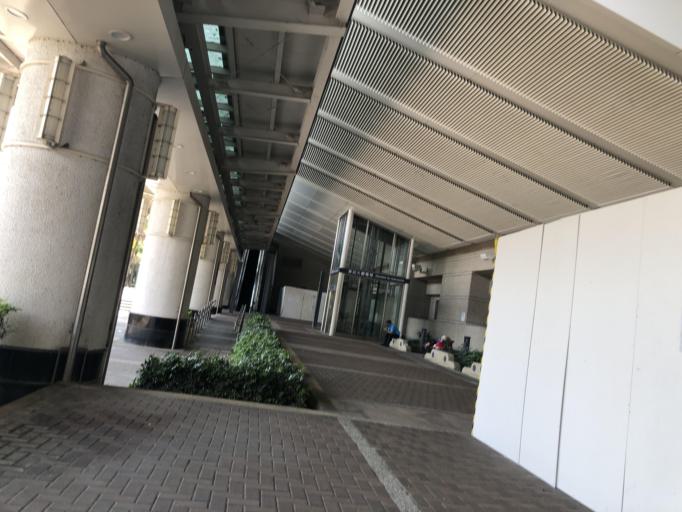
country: TW
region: Kaohsiung
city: Kaohsiung
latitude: 22.6872
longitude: 120.3088
